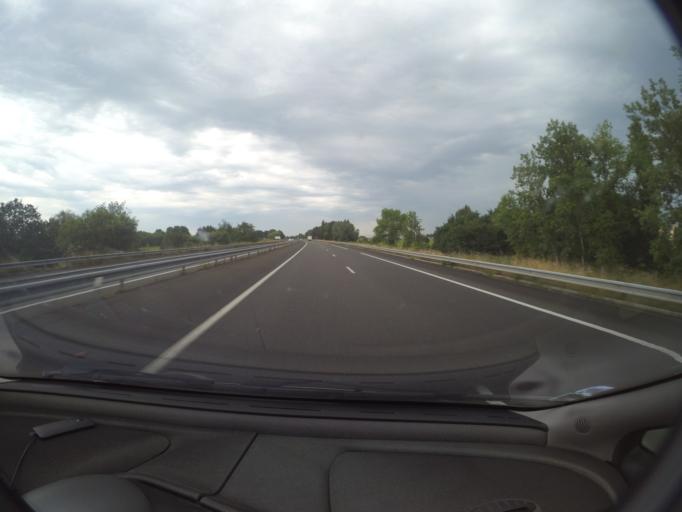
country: FR
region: Pays de la Loire
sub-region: Departement de la Loire-Atlantique
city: Mauves-sur-Loire
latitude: 47.3289
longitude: -1.4023
